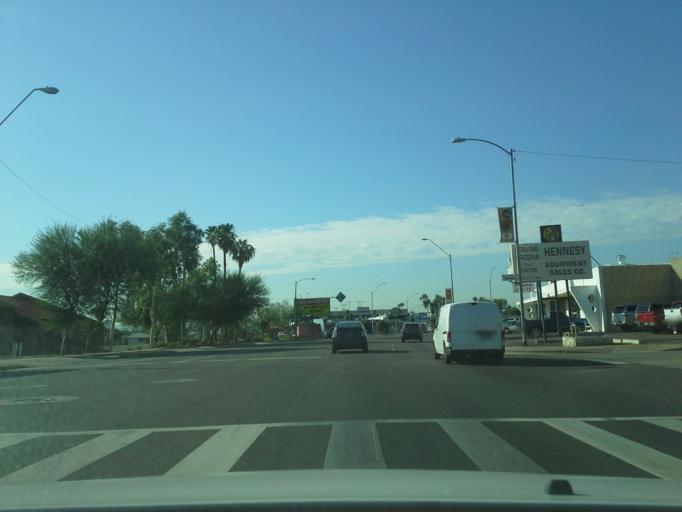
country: US
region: Arizona
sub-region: Maricopa County
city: Phoenix
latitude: 33.5005
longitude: -112.0825
